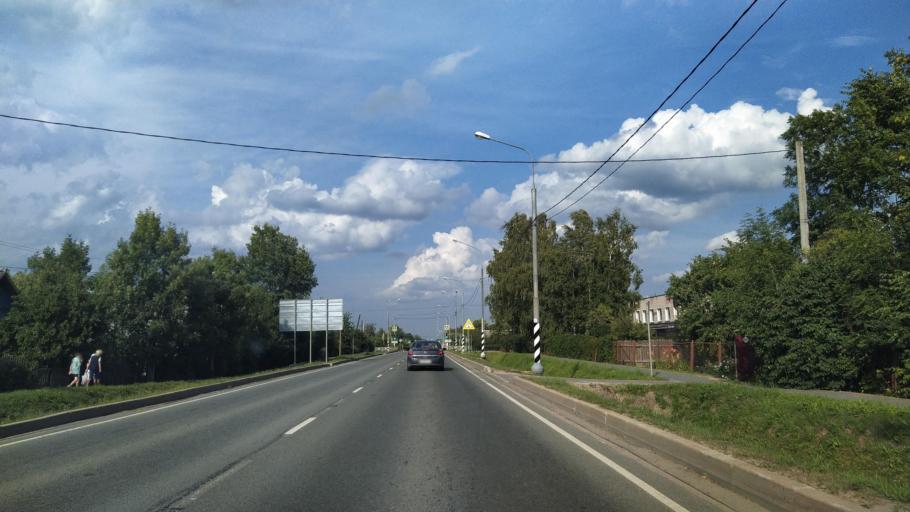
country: RU
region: Novgorod
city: Shimsk
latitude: 58.2108
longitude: 30.7226
